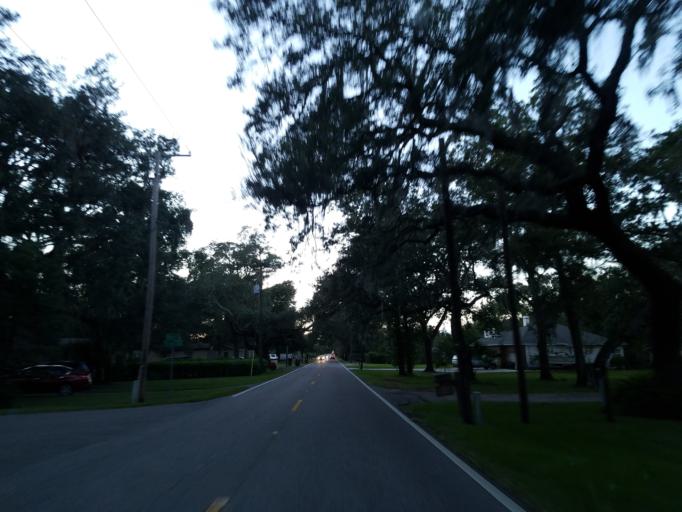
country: US
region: Florida
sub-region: Hillsborough County
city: Bloomingdale
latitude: 27.9161
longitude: -82.2542
